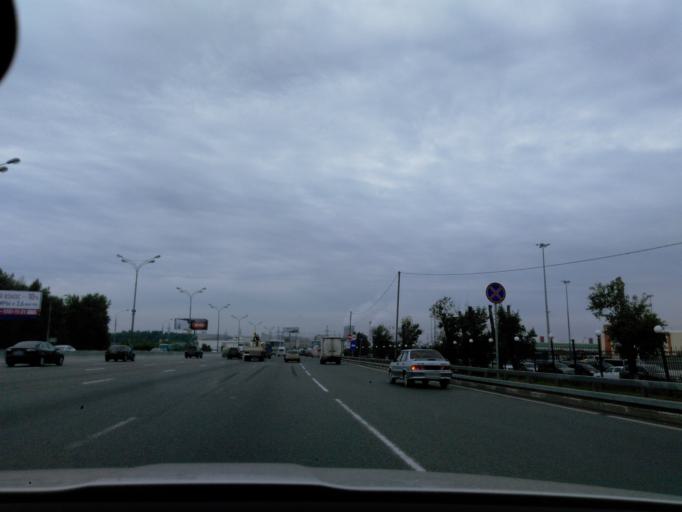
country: RU
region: Moskovskaya
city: Kotel'niki
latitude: 55.6551
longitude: 37.8380
